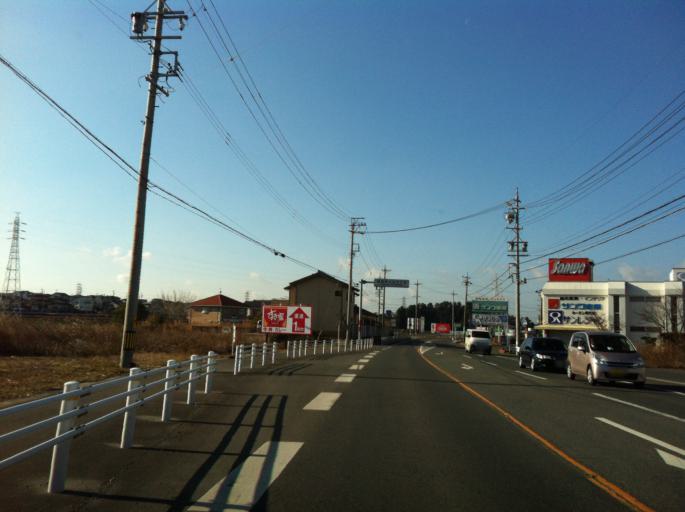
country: JP
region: Aichi
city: Tahara
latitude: 34.6767
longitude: 137.3093
